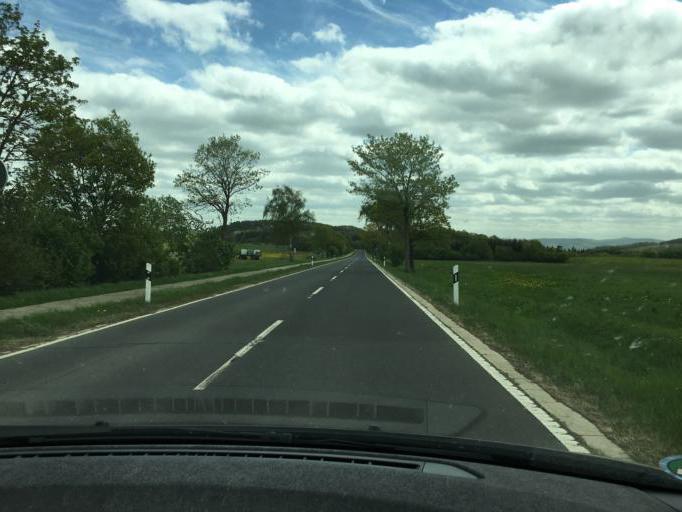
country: DE
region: Rheinland-Pfalz
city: Kirchsahr
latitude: 50.5125
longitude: 6.8760
